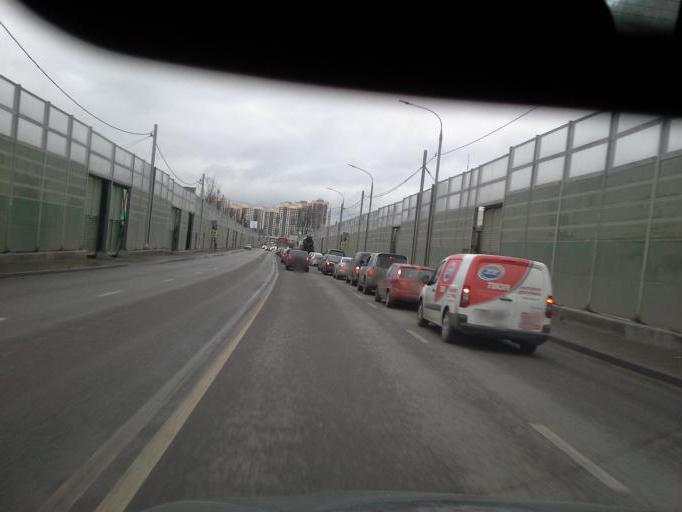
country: RU
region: Moscow
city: Novo-Peredelkino
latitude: 55.6278
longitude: 37.3371
